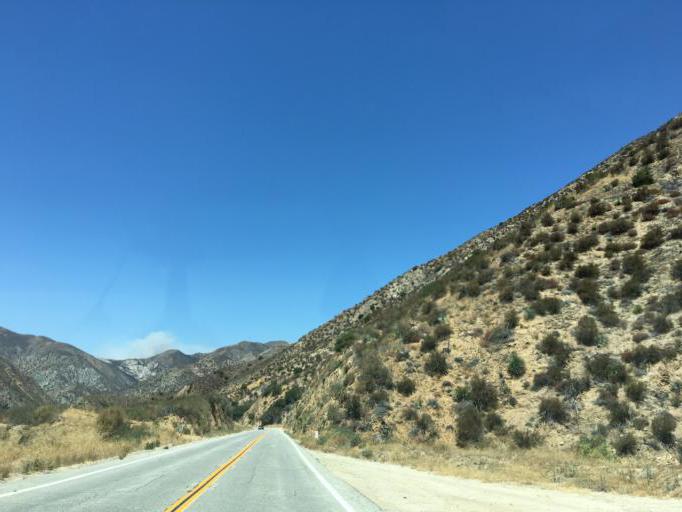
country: US
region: California
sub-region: Los Angeles County
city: La Crescenta-Montrose
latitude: 34.2948
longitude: -118.2369
